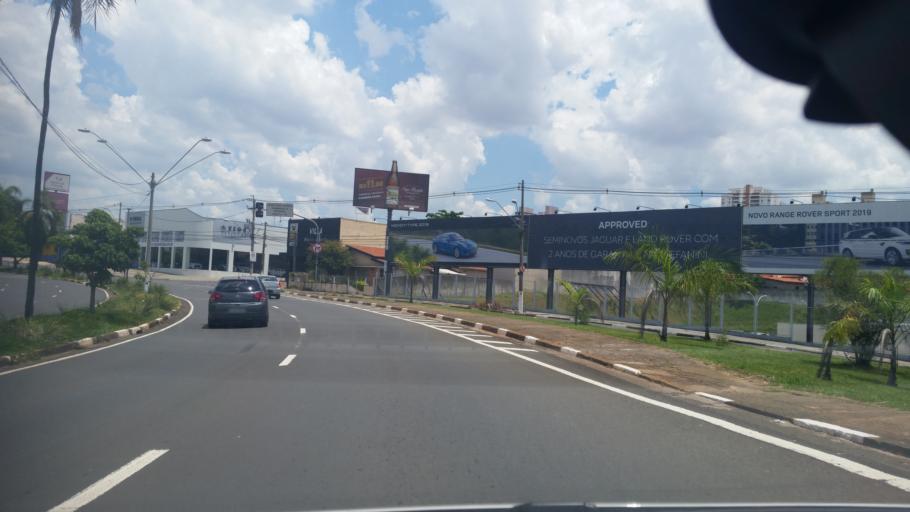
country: BR
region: Sao Paulo
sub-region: Campinas
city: Campinas
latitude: -22.8755
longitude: -47.0463
